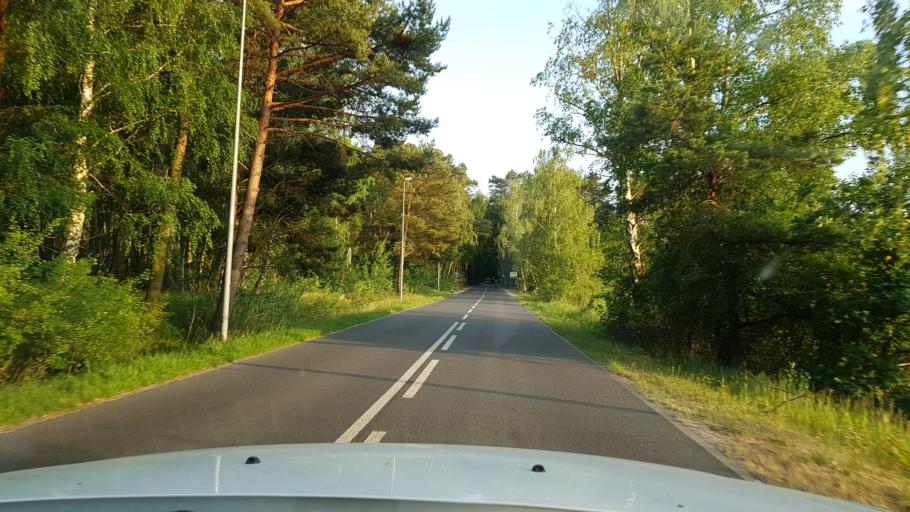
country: PL
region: West Pomeranian Voivodeship
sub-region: Swinoujscie
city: Swinoujscie
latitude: 53.8550
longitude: 14.2859
